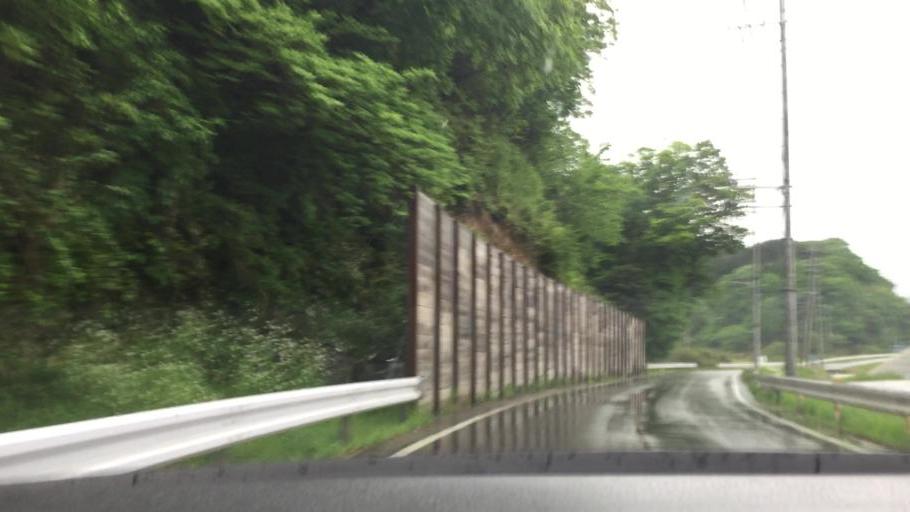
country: JP
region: Hyogo
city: Toyooka
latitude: 35.4814
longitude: 134.8105
